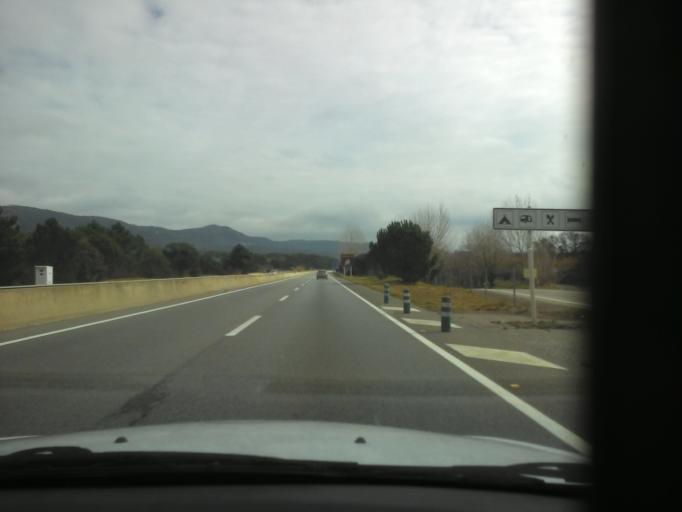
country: ES
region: Catalonia
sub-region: Provincia de Girona
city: Santa Cristina d'Aro
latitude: 41.8274
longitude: 2.9593
